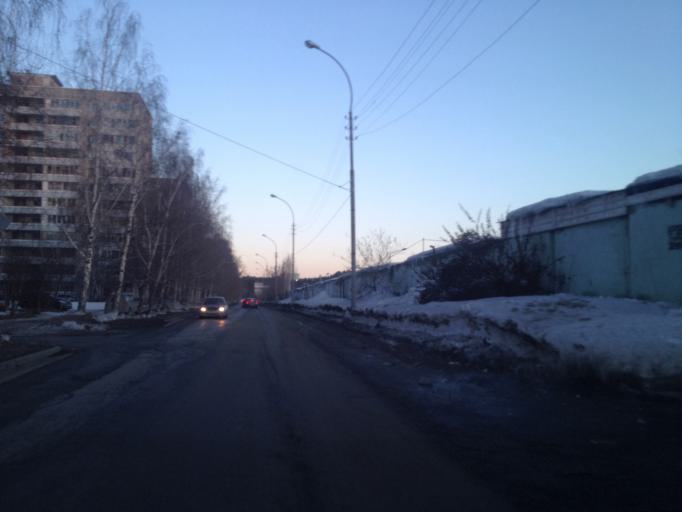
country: RU
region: Sverdlovsk
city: Sovkhoznyy
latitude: 56.7939
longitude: 60.5689
